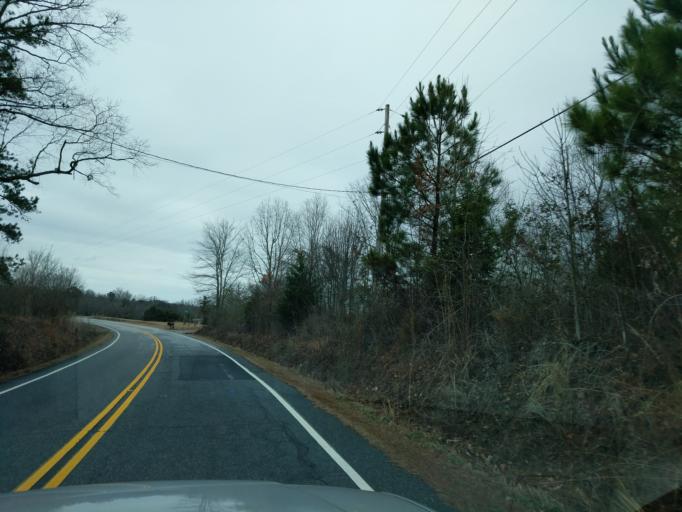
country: US
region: South Carolina
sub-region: Oconee County
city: Walhalla
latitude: 34.8233
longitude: -83.0460
